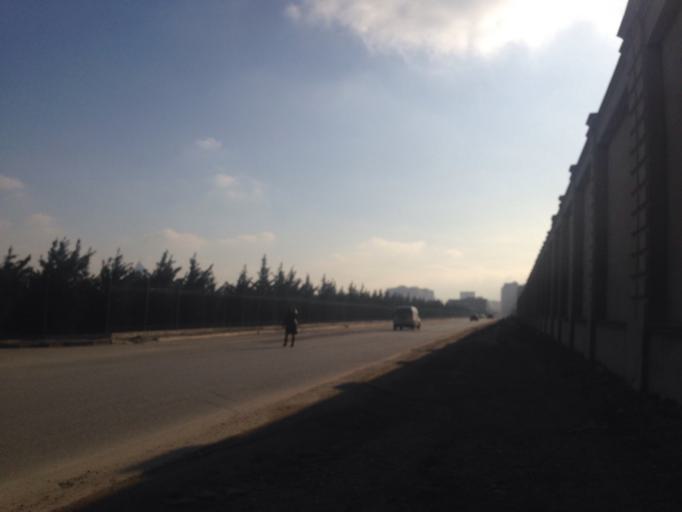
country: AZ
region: Baki
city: Baku
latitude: 40.4090
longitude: 49.8557
